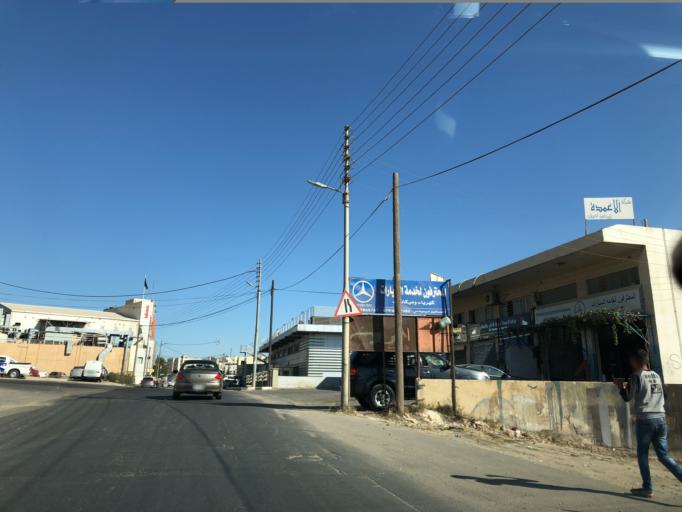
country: JO
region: Amman
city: Wadi as Sir
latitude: 31.9408
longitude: 35.8479
